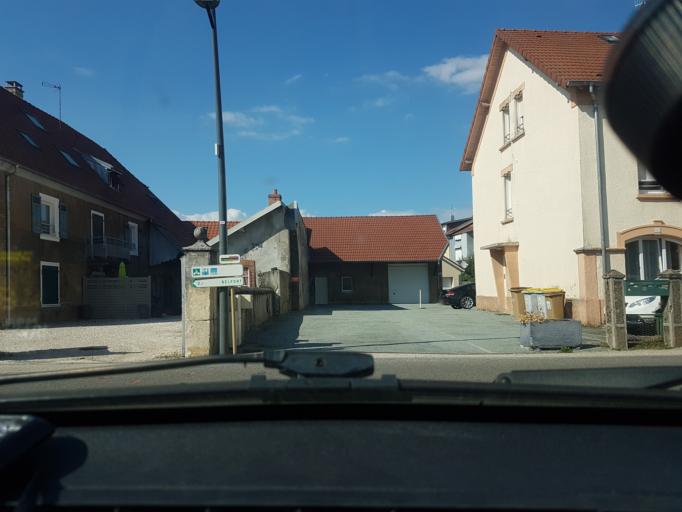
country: FR
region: Franche-Comte
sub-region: Territoire de Belfort
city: Danjoutin
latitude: 47.6181
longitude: 6.8651
